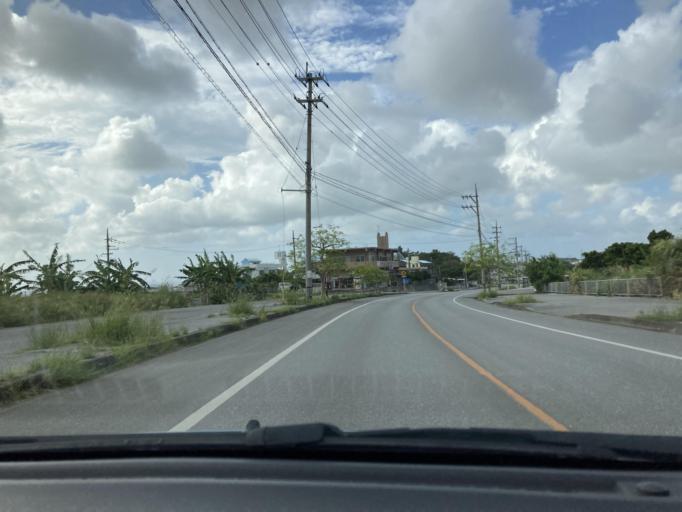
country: JP
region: Okinawa
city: Itoman
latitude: 26.1251
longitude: 127.6923
